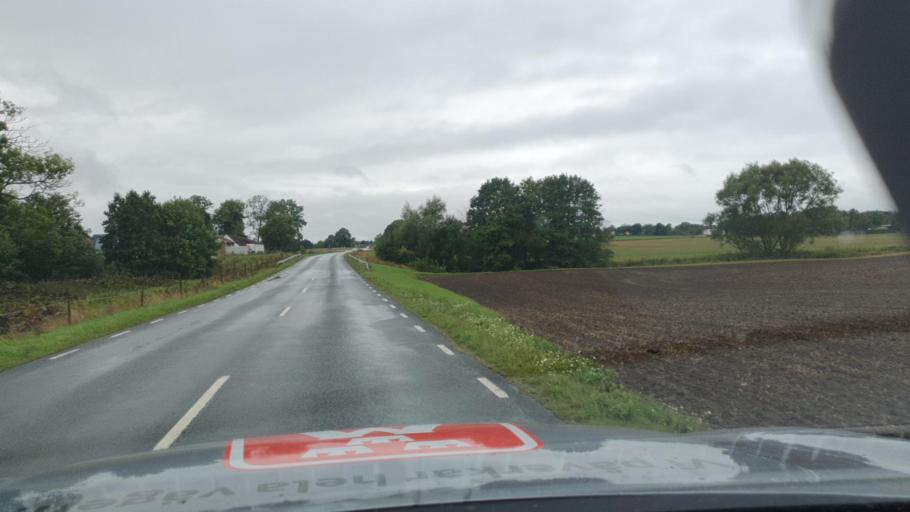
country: SE
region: Skane
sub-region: Simrishamns Kommun
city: Kivik
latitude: 55.5809
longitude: 14.1303
